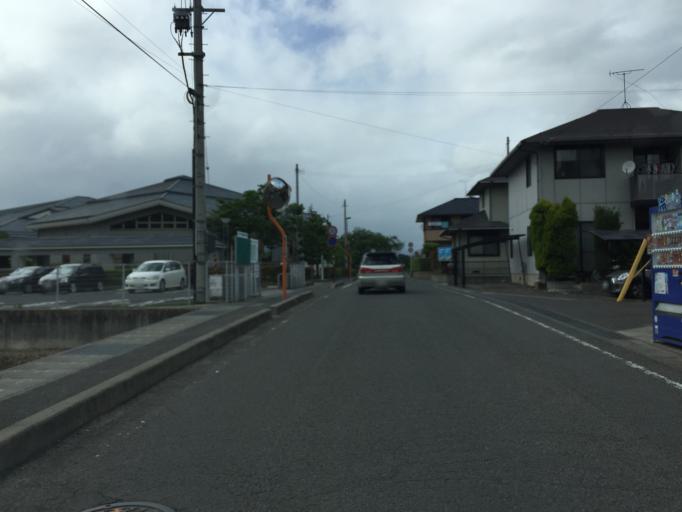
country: JP
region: Fukushima
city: Fukushima-shi
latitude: 37.7801
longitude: 140.4578
